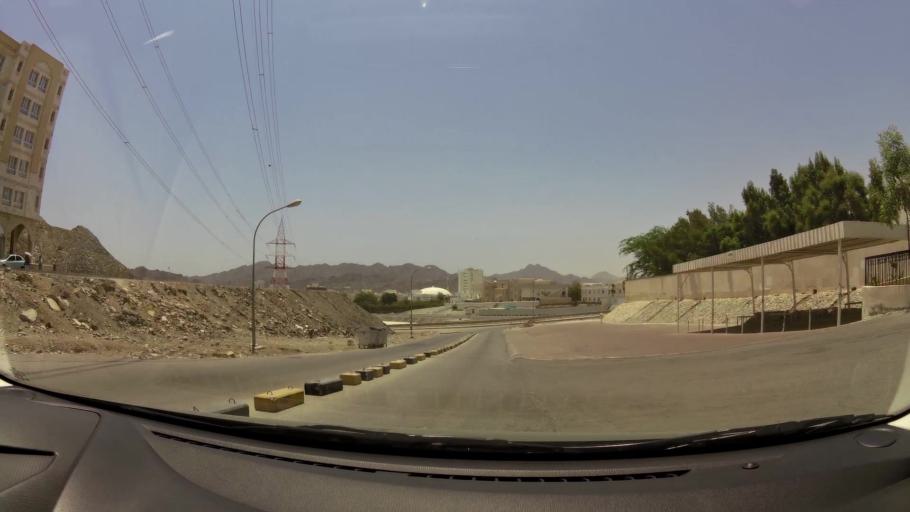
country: OM
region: Muhafazat Masqat
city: Muscat
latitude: 23.6079
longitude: 58.5344
